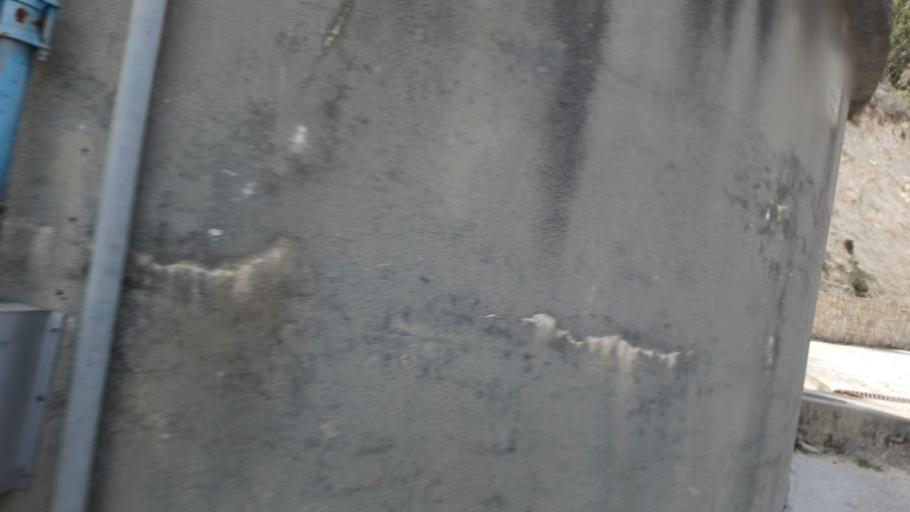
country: CY
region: Limassol
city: Pachna
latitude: 34.7778
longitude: 32.7375
